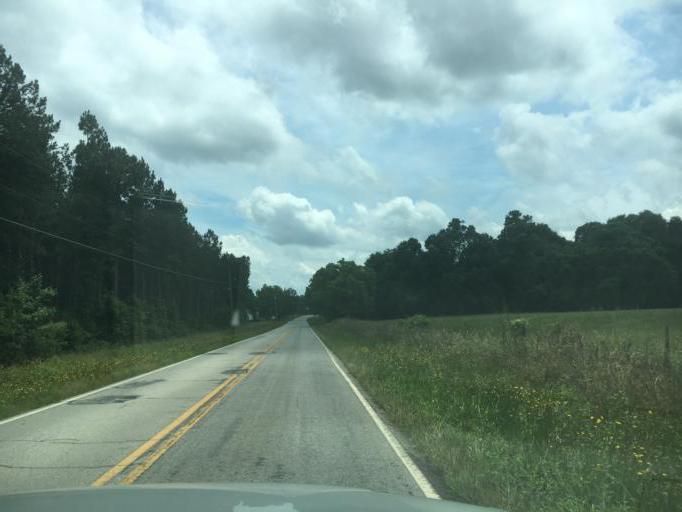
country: US
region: Georgia
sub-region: Hart County
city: Reed Creek
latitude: 34.4279
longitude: -82.9516
